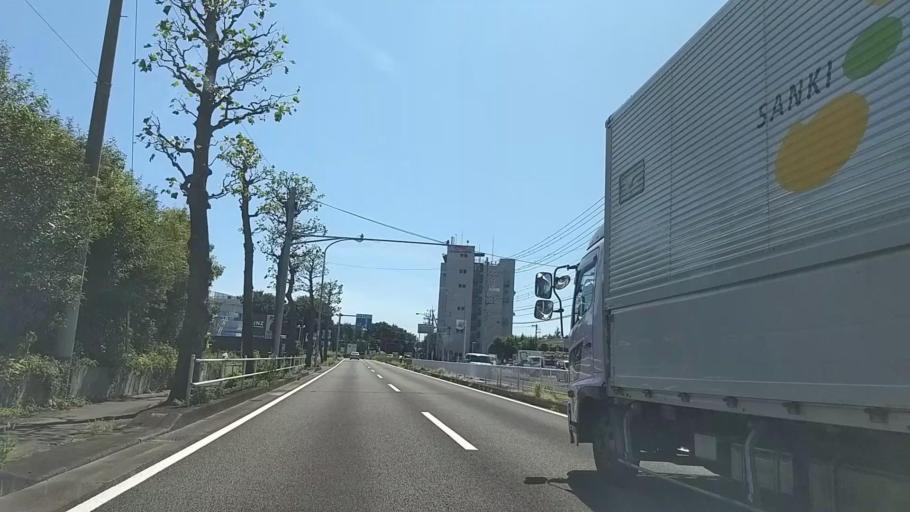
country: JP
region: Kanagawa
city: Zama
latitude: 35.5434
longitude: 139.3596
